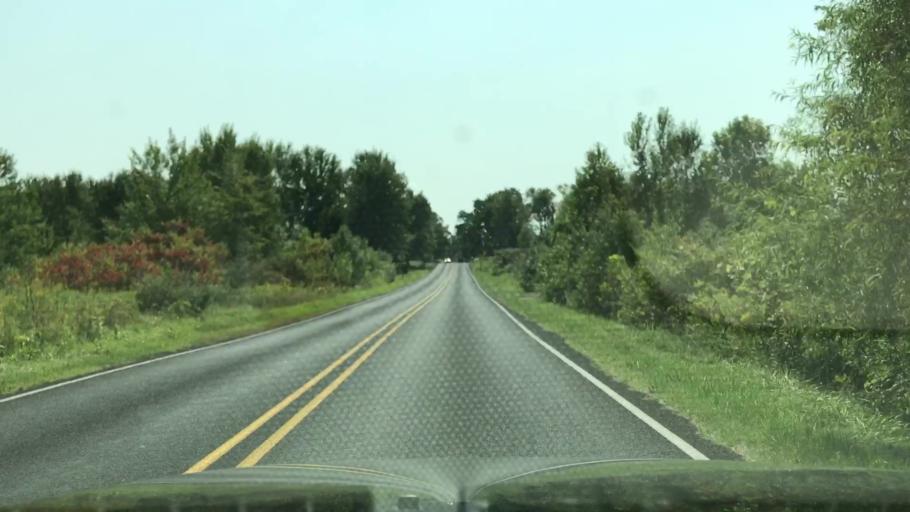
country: US
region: Michigan
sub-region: Kent County
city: Byron Center
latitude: 42.8150
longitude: -85.7829
